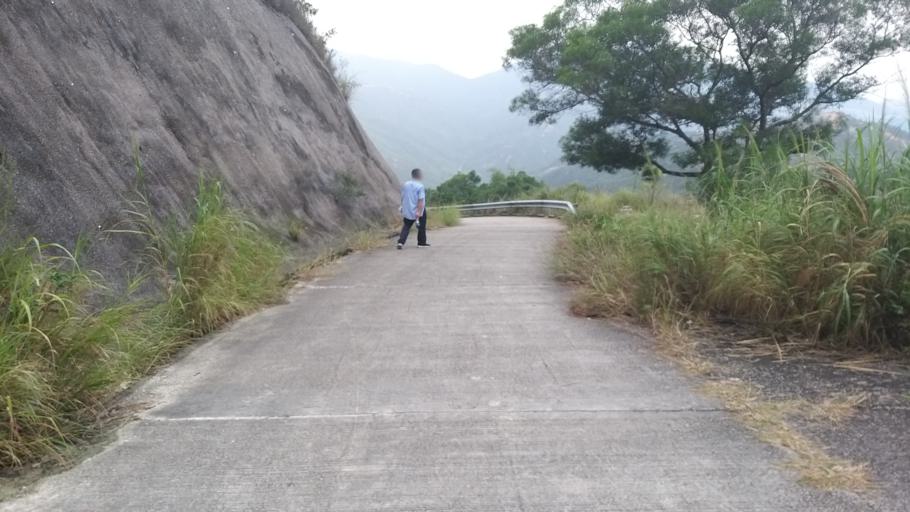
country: HK
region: Tuen Mun
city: Tuen Mun
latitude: 22.4094
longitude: 113.9531
